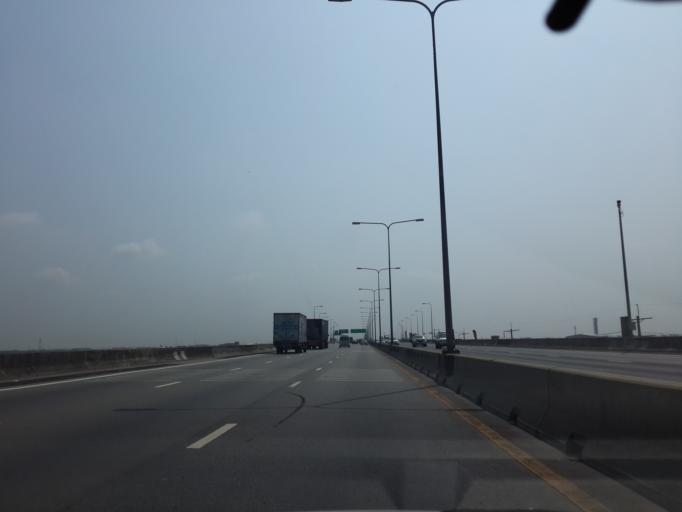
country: TH
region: Samut Prakan
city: Bang Bo
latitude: 13.5766
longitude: 100.8907
